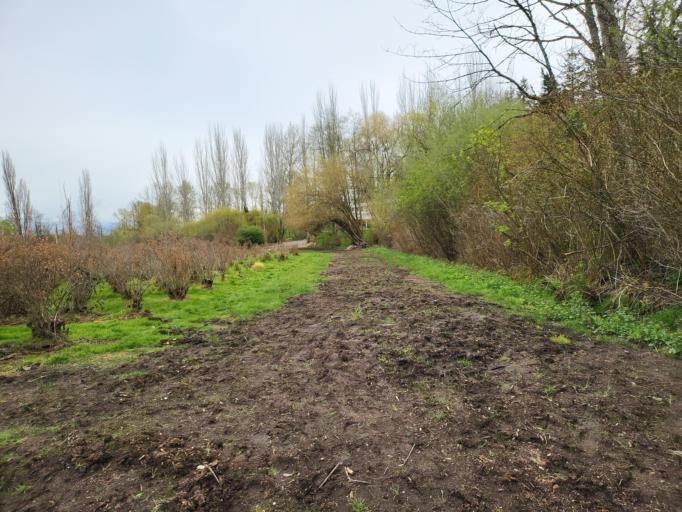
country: US
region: Washington
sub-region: King County
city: Newport
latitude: 47.5901
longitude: -122.1911
